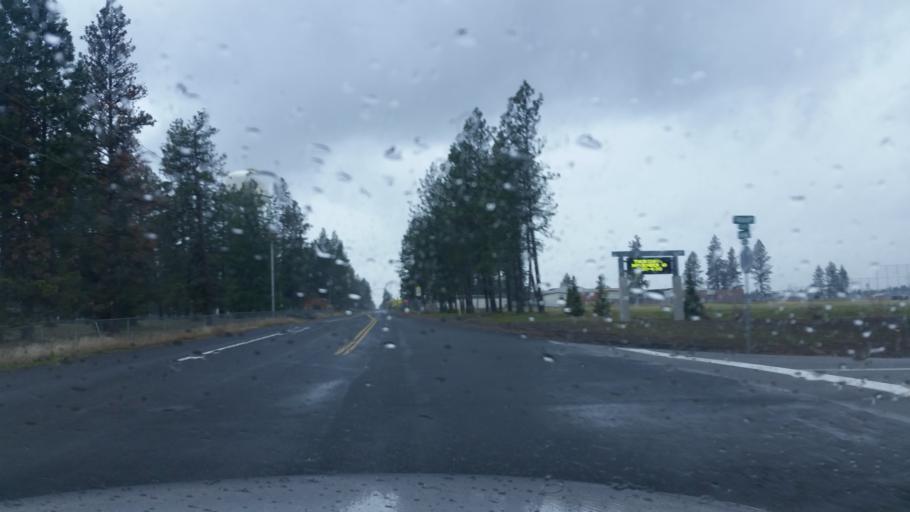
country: US
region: Washington
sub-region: Spokane County
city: Spokane
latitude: 47.5945
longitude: -117.4862
